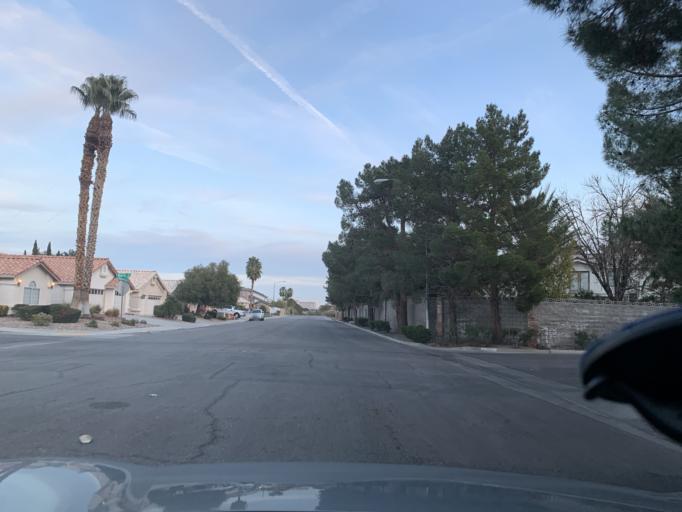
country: US
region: Nevada
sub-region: Clark County
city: Spring Valley
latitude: 36.0907
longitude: -115.2320
